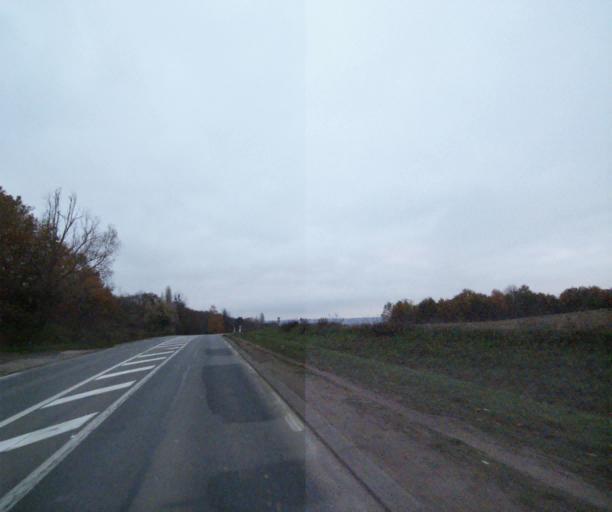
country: FR
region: Ile-de-France
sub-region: Departement des Yvelines
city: Villennes-sur-Seine
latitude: 48.9429
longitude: 1.9782
